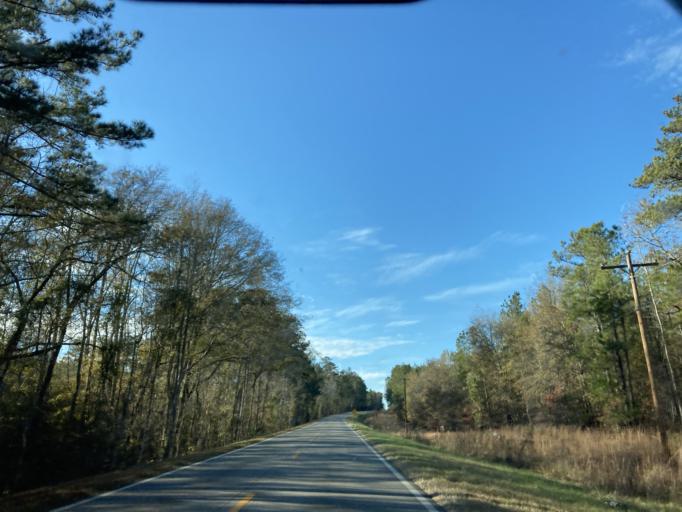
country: US
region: Georgia
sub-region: Jones County
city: Gray
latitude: 32.8886
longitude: -83.5009
